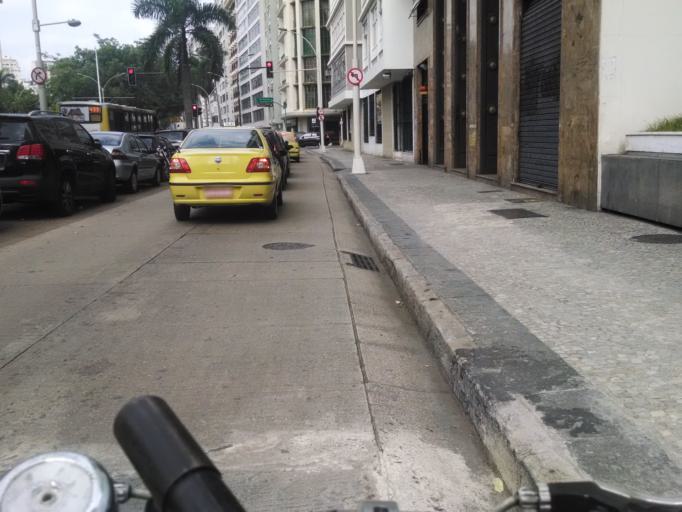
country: BR
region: Rio de Janeiro
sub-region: Rio De Janeiro
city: Rio de Janeiro
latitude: -22.9325
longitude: -43.1746
